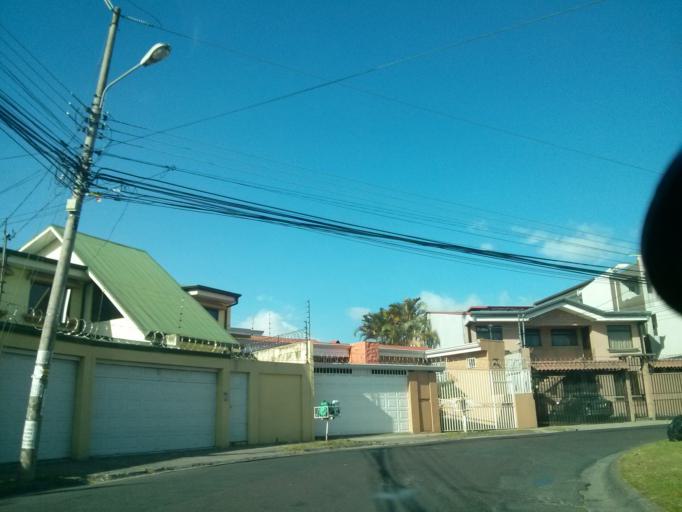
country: CR
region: San Jose
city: Sabanilla
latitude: 9.9323
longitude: -84.0385
